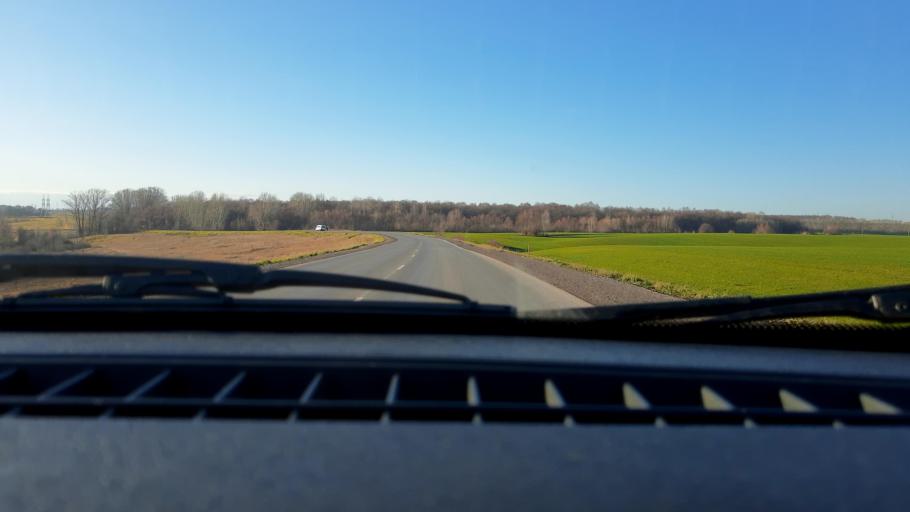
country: RU
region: Bashkortostan
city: Mikhaylovka
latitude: 54.8330
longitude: 55.9416
